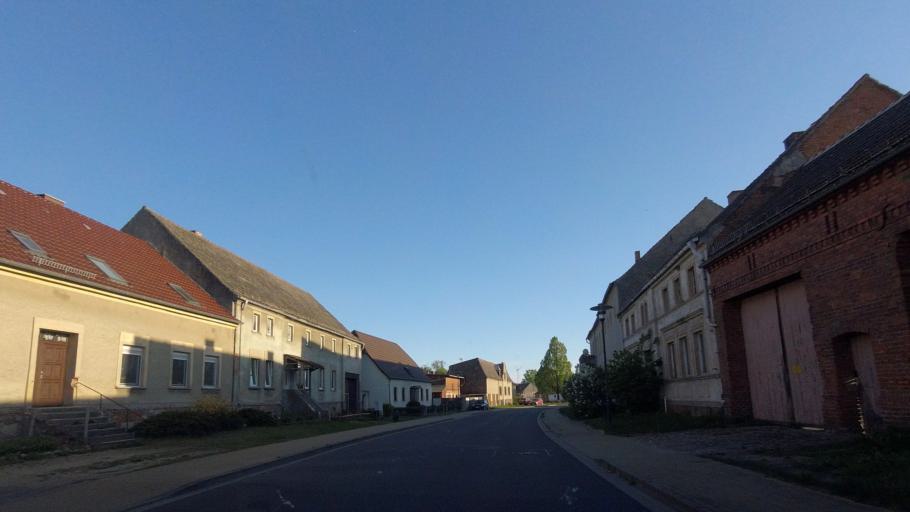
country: DE
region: Brandenburg
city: Ihlow
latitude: 51.9885
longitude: 13.3566
